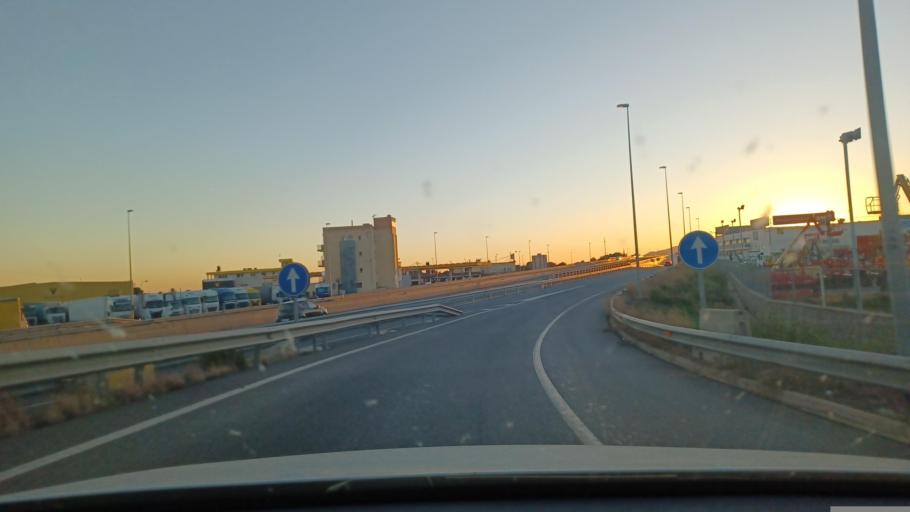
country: ES
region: Catalonia
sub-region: Provincia de Tarragona
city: Vila-seca
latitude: 41.1046
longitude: 1.1305
